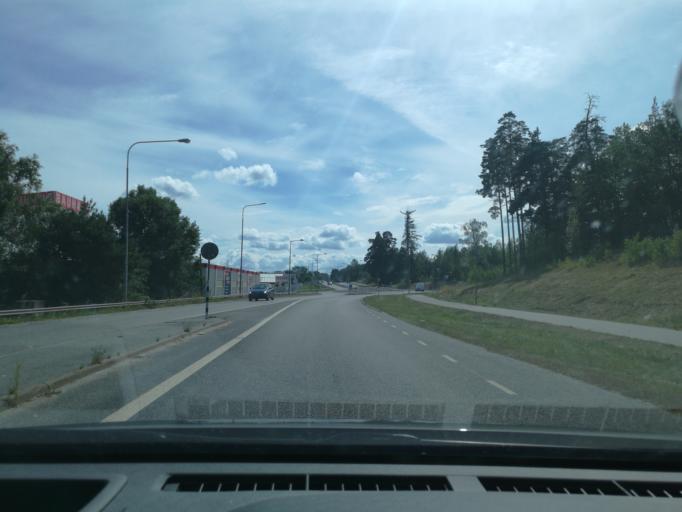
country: SE
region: Stockholm
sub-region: Upplands Vasby Kommun
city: Upplands Vaesby
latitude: 59.5025
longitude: 17.9228
